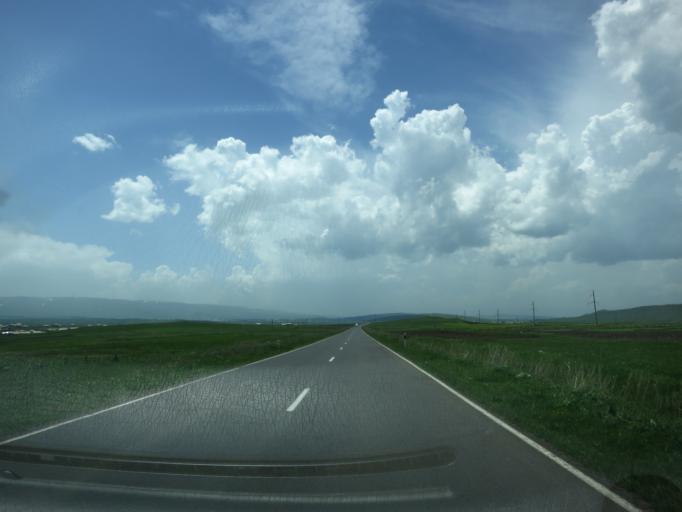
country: GE
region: Samtskhe-Javakheti
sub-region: Ninotsminda
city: Ninotsminda
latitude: 41.2963
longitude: 43.6674
